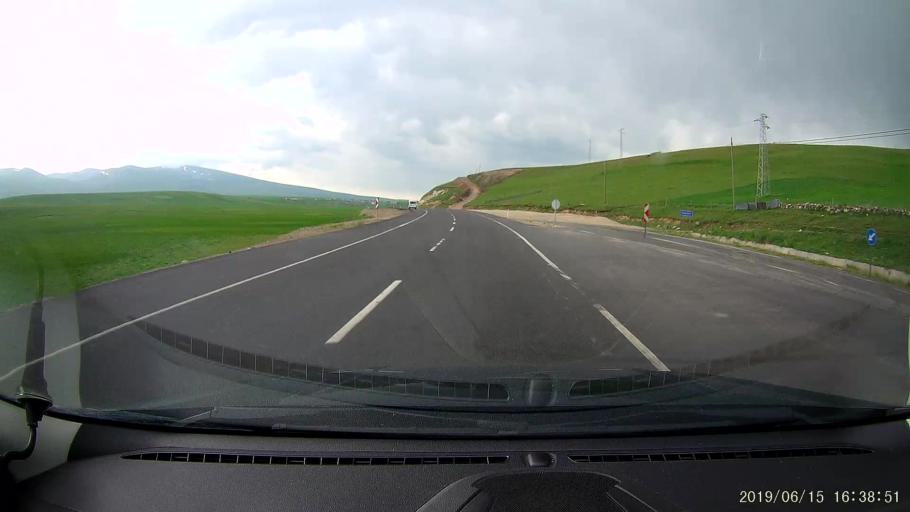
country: TR
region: Ardahan
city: Haskoy
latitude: 40.9885
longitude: 42.8914
